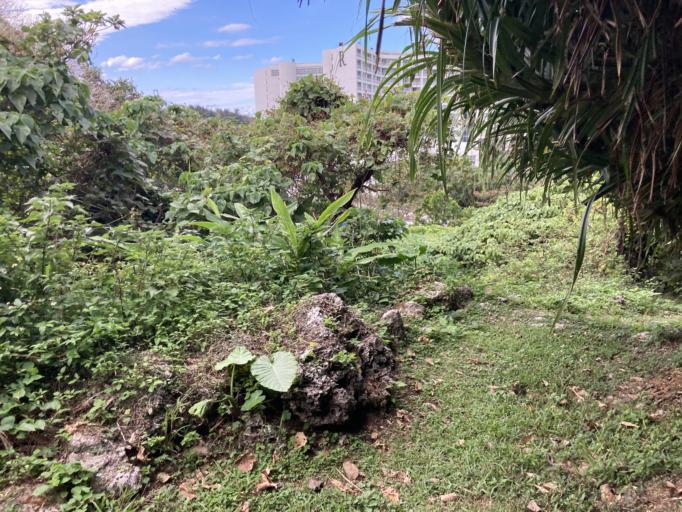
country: JP
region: Okinawa
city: Ishikawa
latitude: 26.4348
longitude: 127.7898
